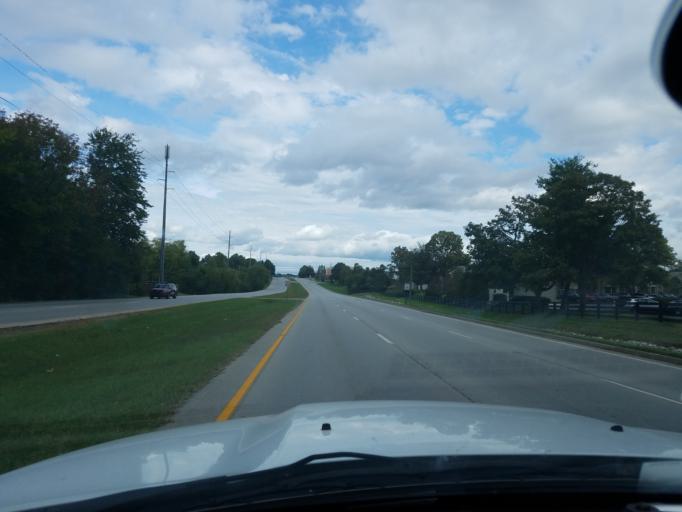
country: US
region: Kentucky
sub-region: Jefferson County
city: Hurstbourne
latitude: 38.2303
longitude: -85.5772
